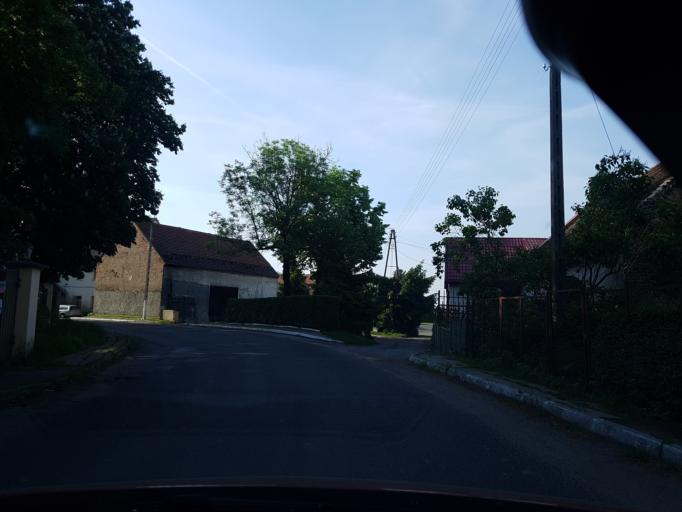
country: PL
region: Lower Silesian Voivodeship
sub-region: Powiat strzelinski
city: Wiazow
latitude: 50.8550
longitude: 17.1857
